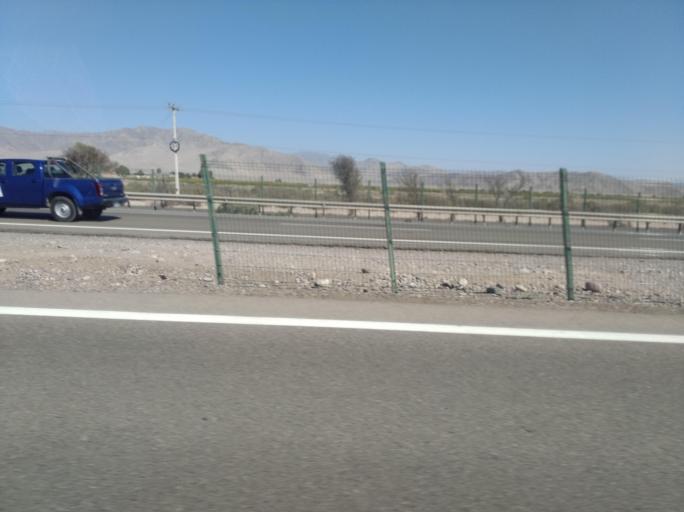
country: CL
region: Atacama
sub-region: Provincia de Copiapo
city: Copiapo
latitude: -27.3375
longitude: -70.5962
